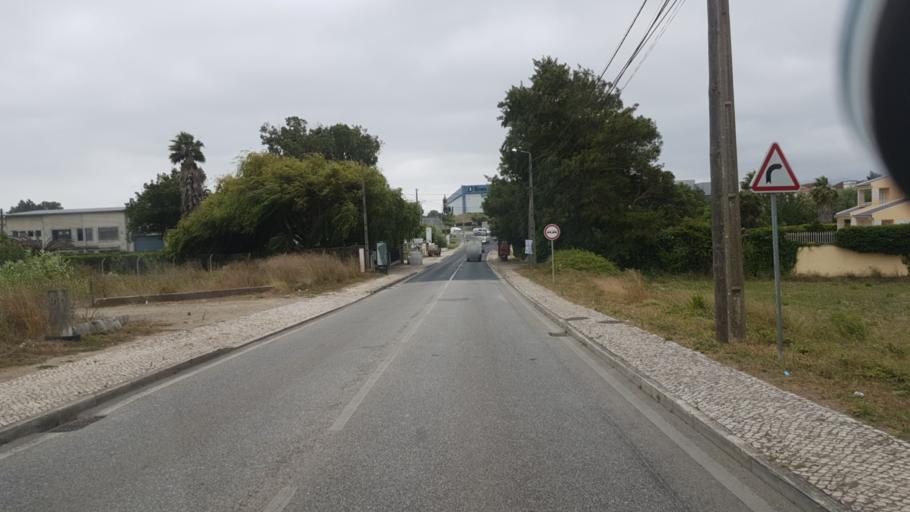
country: PT
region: Lisbon
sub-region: Sintra
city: Pero Pinheiro
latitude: 38.8506
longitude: -9.3268
